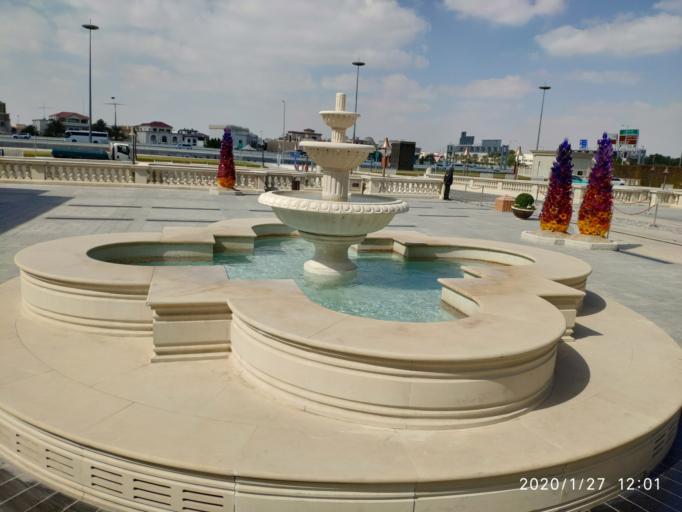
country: QA
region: Baladiyat ad Dawhah
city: Doha
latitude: 25.3616
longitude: 51.5225
